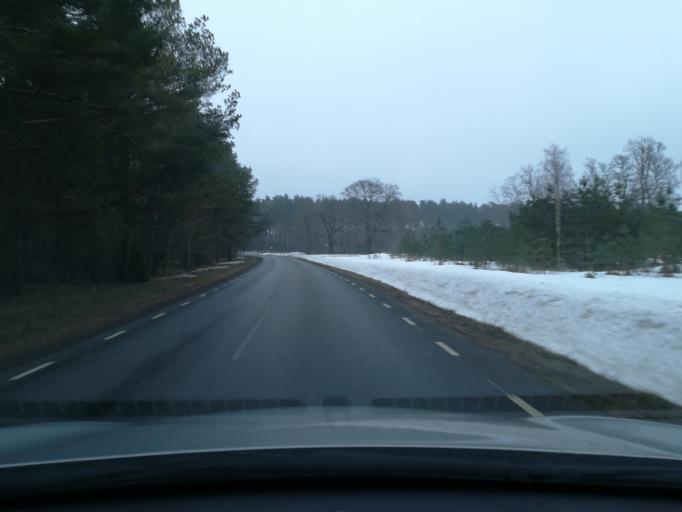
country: EE
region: Harju
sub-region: Kuusalu vald
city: Kuusalu
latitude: 59.4586
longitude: 25.4725
